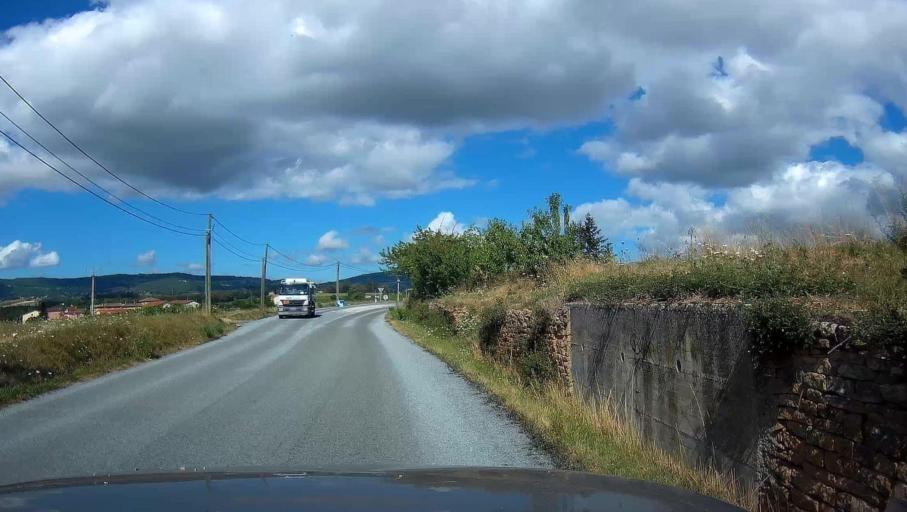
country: FR
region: Rhone-Alpes
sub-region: Departement du Rhone
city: Liergues
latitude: 45.9722
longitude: 4.6559
